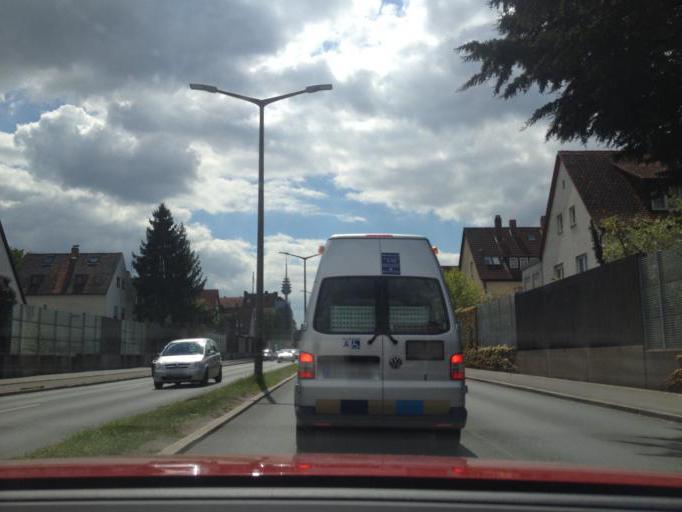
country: DE
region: Bavaria
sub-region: Regierungsbezirk Mittelfranken
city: Grossreuth bei Schweinau
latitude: 49.4428
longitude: 11.0358
